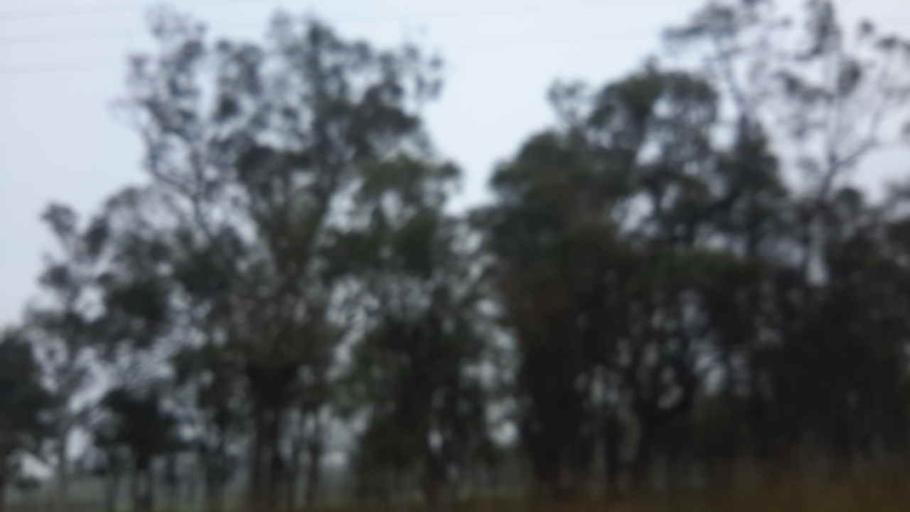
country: AU
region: New South Wales
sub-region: Penrith Municipality
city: Werrington Downs
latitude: -33.6761
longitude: 150.7465
